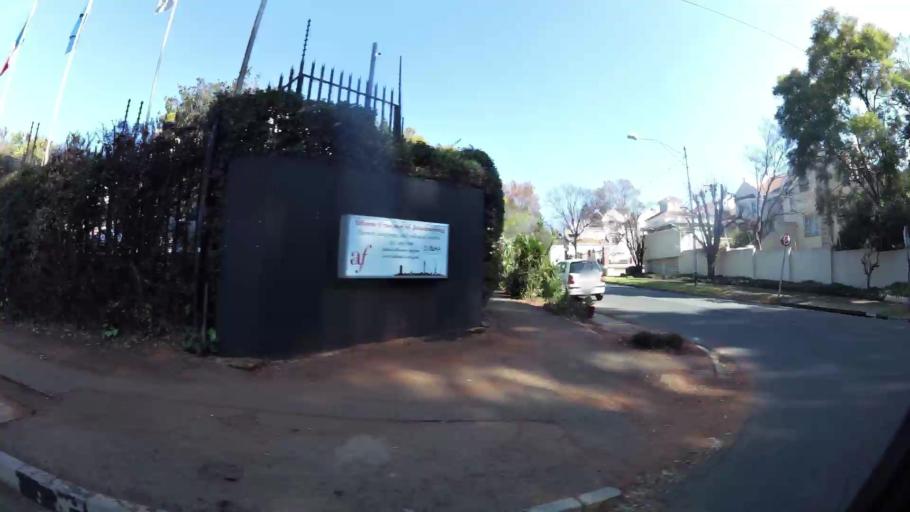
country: ZA
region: Gauteng
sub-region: City of Johannesburg Metropolitan Municipality
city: Johannesburg
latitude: -26.1631
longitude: 28.0312
